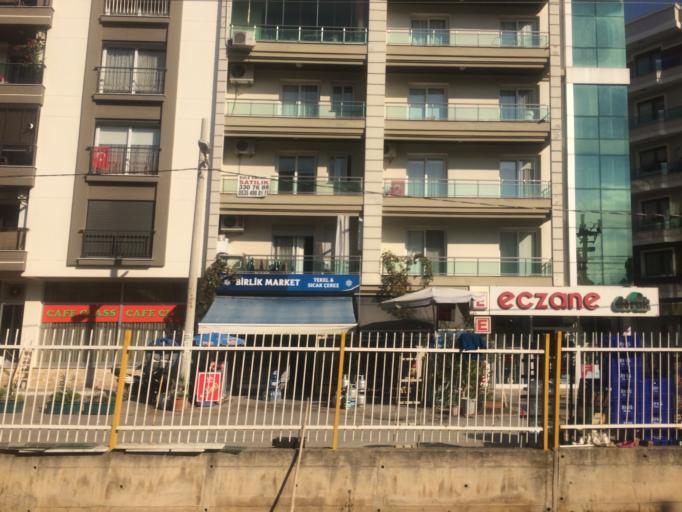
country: TR
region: Izmir
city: Karsiyaka
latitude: 38.4718
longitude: 27.0930
